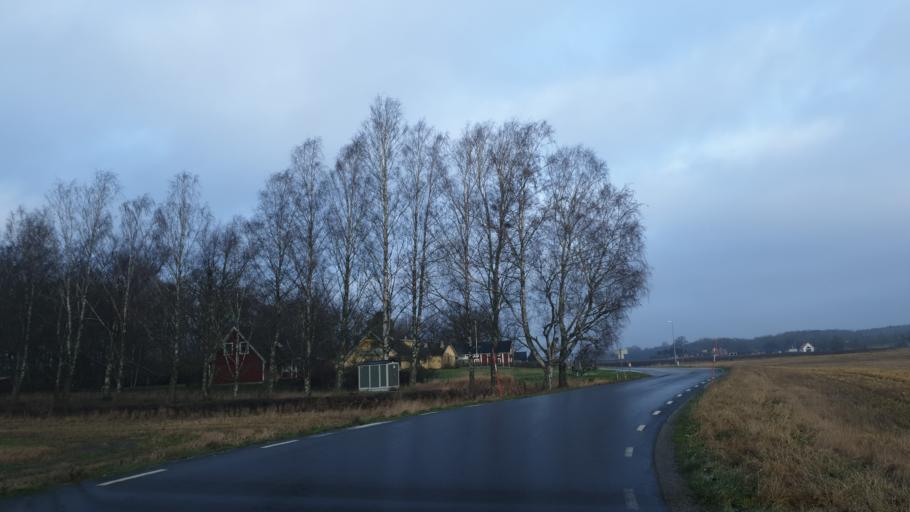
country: SE
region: Blekinge
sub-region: Karlshamns Kommun
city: Morrum
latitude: 56.1646
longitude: 14.7480
